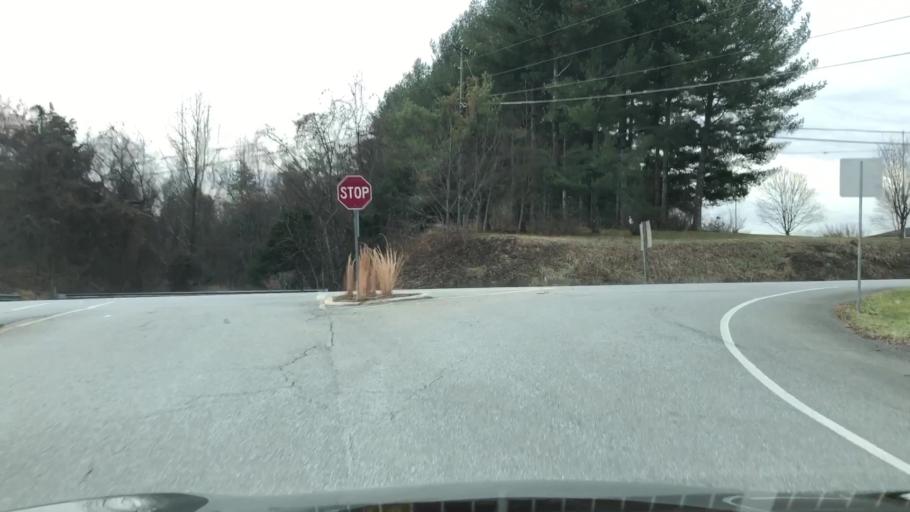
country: US
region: Virginia
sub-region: City of Lynchburg
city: West Lynchburg
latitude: 37.4160
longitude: -79.2333
